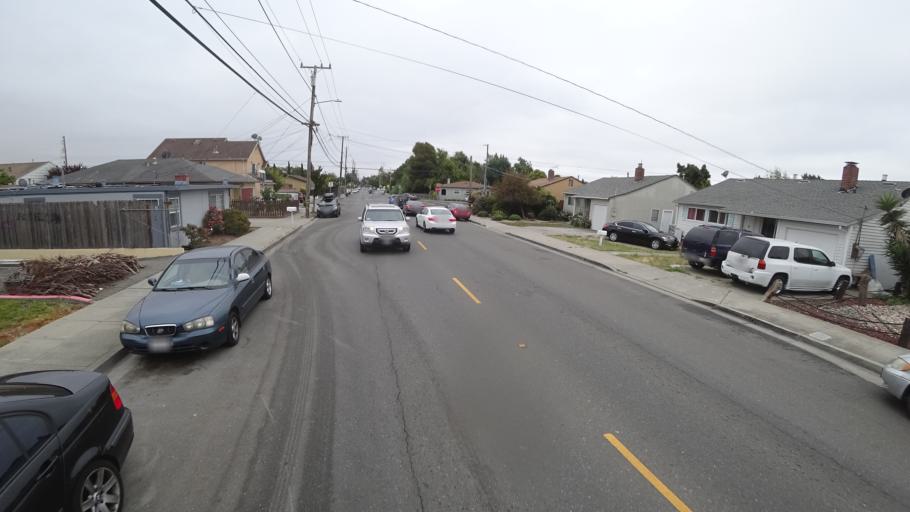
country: US
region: California
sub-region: Alameda County
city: Hayward
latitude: 37.6260
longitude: -122.0662
